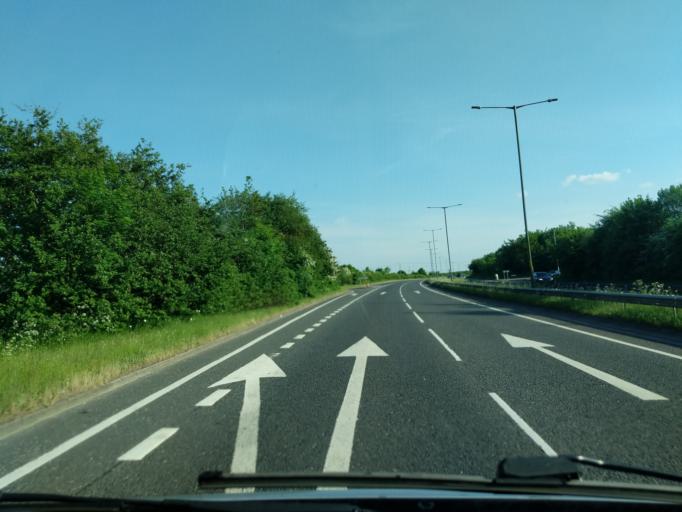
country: GB
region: England
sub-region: St. Helens
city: St Helens
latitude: 53.4127
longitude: -2.7444
